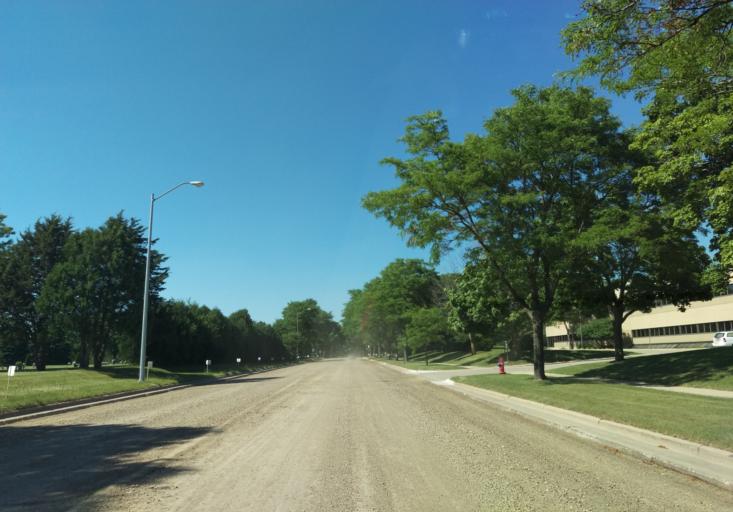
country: US
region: Wisconsin
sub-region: Dane County
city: Middleton
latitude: 43.0621
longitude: -89.5077
